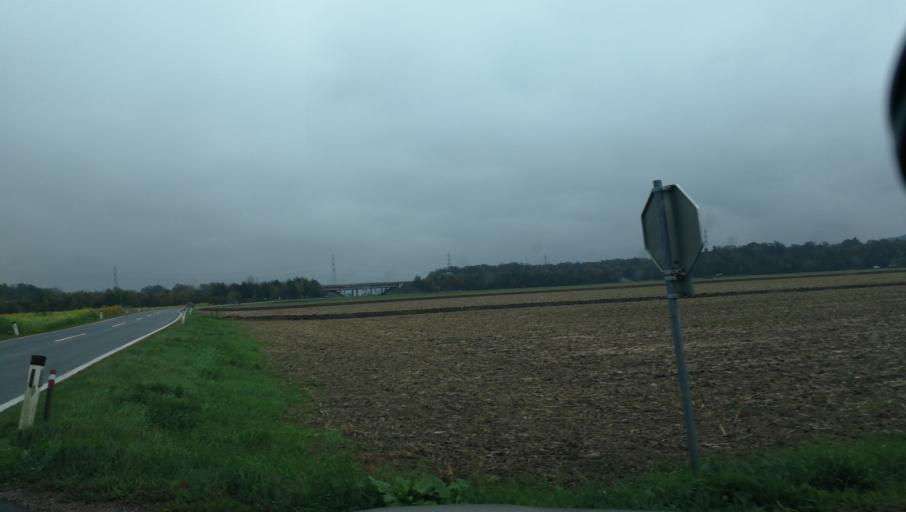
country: AT
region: Styria
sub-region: Politischer Bezirk Leibnitz
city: Strass in Steiermark
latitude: 46.7255
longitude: 15.6399
